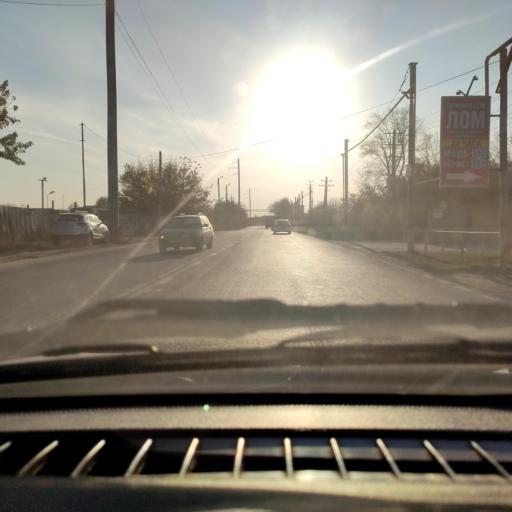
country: RU
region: Samara
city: Tol'yatti
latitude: 53.5285
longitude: 49.4758
